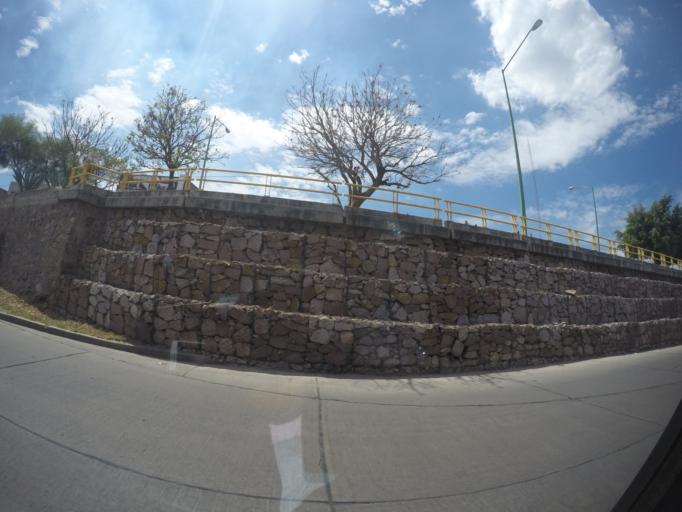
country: MX
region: Guanajuato
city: Leon
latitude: 21.1325
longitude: -101.6782
